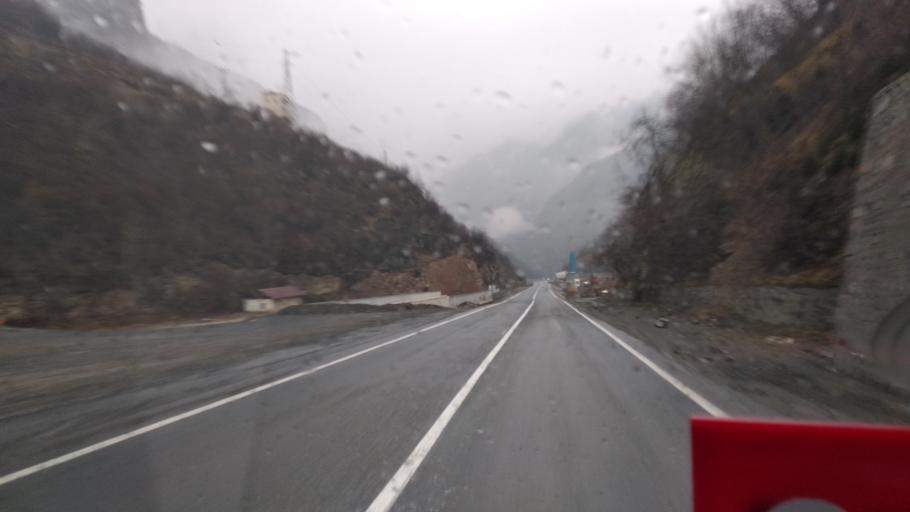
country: TR
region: Trabzon
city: Macka
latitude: 40.7407
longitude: 39.5506
